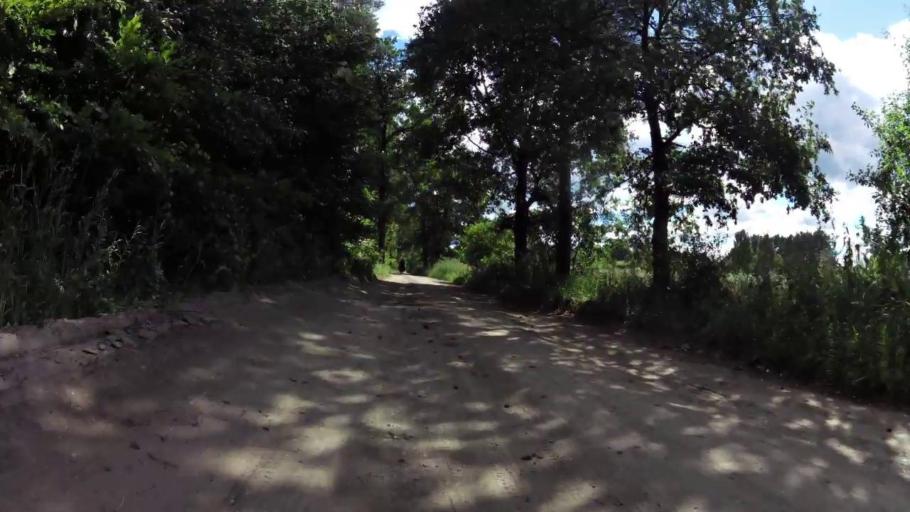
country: PL
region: West Pomeranian Voivodeship
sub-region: Powiat lobeski
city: Lobez
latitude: 53.6669
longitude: 15.5532
